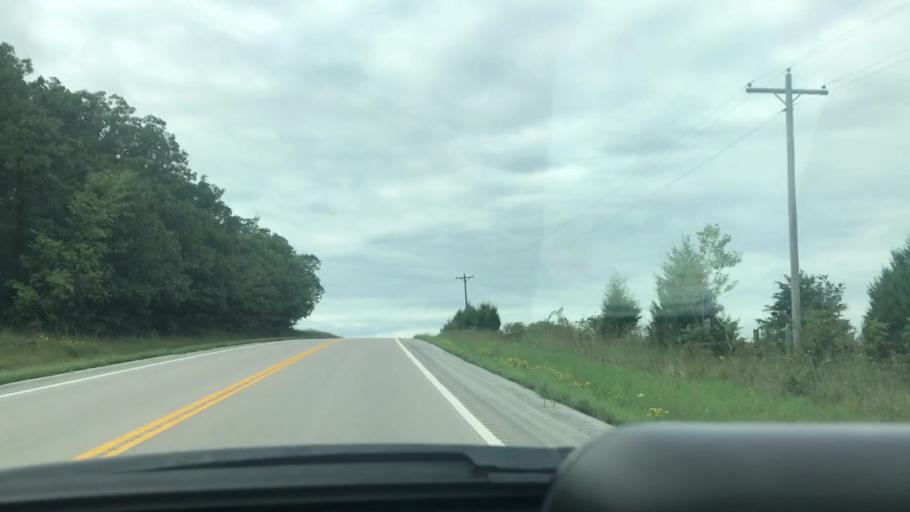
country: US
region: Missouri
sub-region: Benton County
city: Warsaw
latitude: 38.1426
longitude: -93.2885
